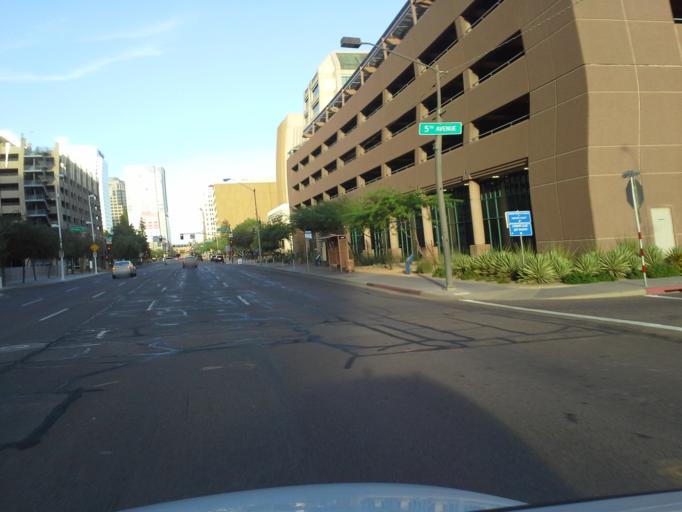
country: US
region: Arizona
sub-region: Maricopa County
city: Phoenix
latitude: 33.4471
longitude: -112.0803
